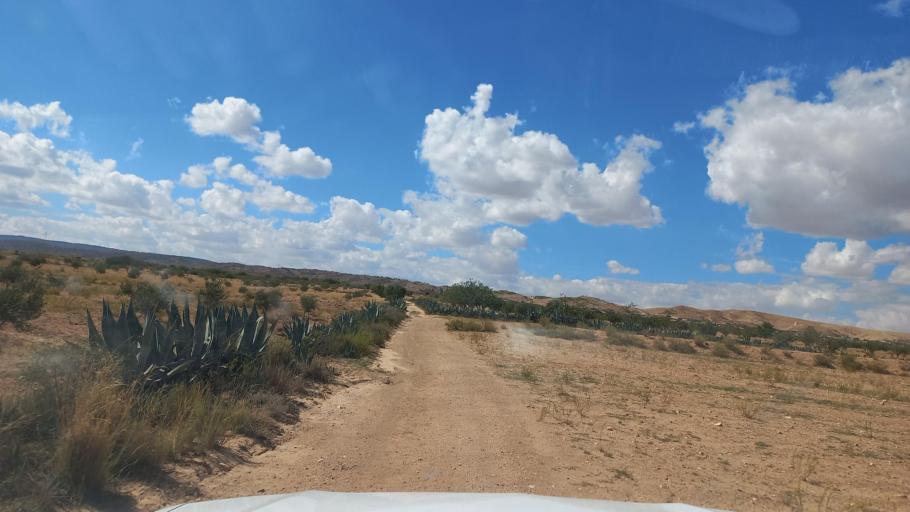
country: TN
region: Al Qasrayn
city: Sbiba
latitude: 35.3648
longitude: 9.0207
